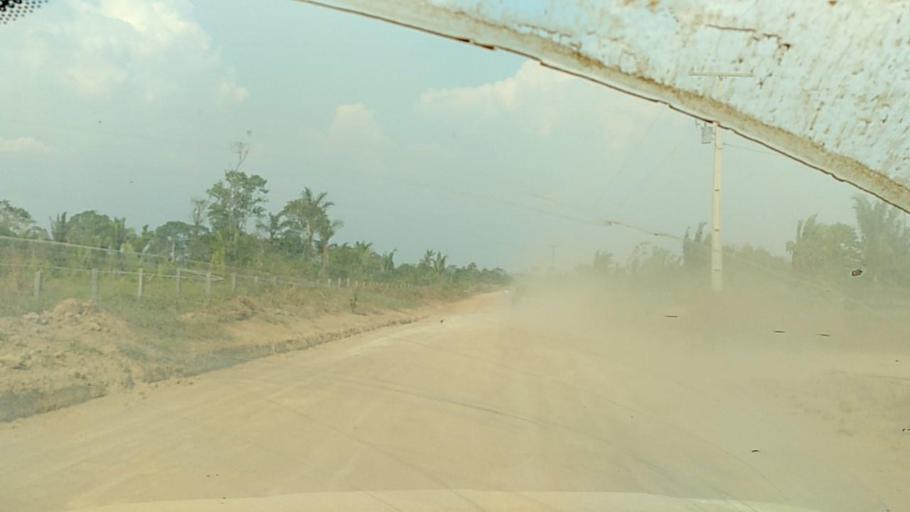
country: BR
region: Rondonia
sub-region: Porto Velho
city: Porto Velho
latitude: -8.6832
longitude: -63.1953
